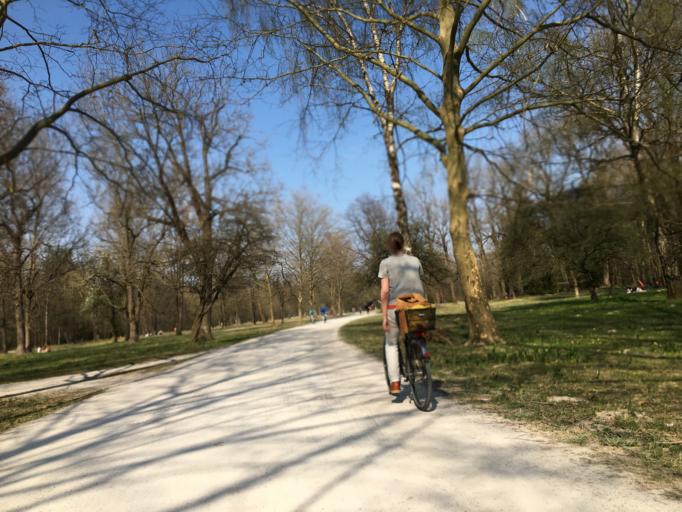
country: DE
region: Bavaria
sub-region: Upper Bavaria
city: Bogenhausen
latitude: 48.1753
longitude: 11.6182
